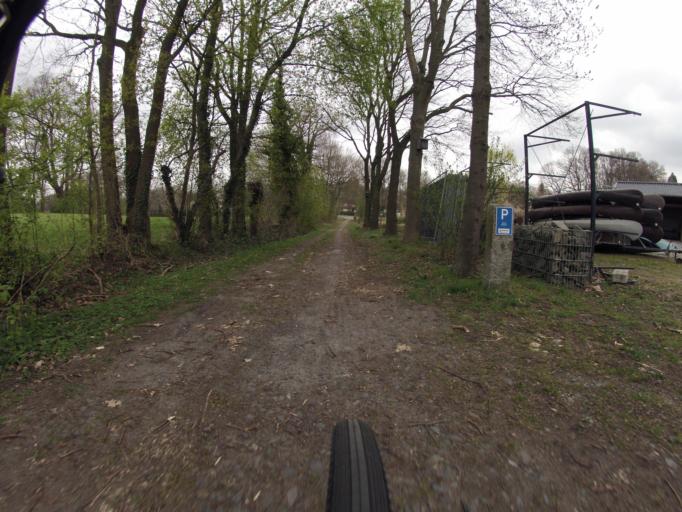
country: DE
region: North Rhine-Westphalia
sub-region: Regierungsbezirk Munster
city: Mettingen
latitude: 52.3216
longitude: 7.7663
